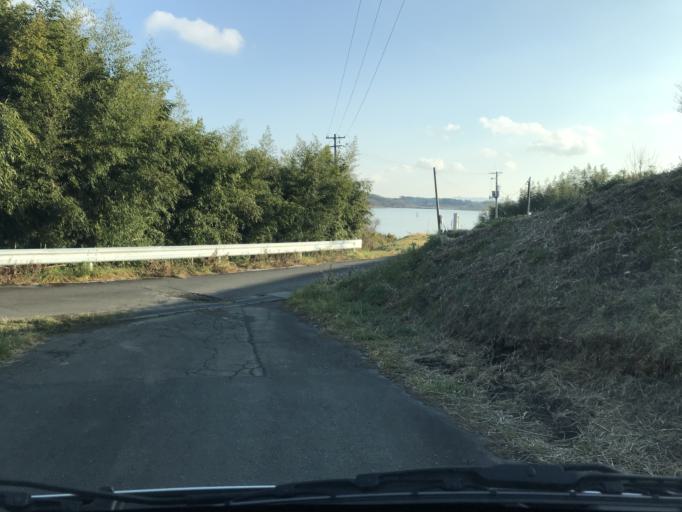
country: JP
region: Miyagi
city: Wakuya
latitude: 38.6943
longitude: 141.1209
